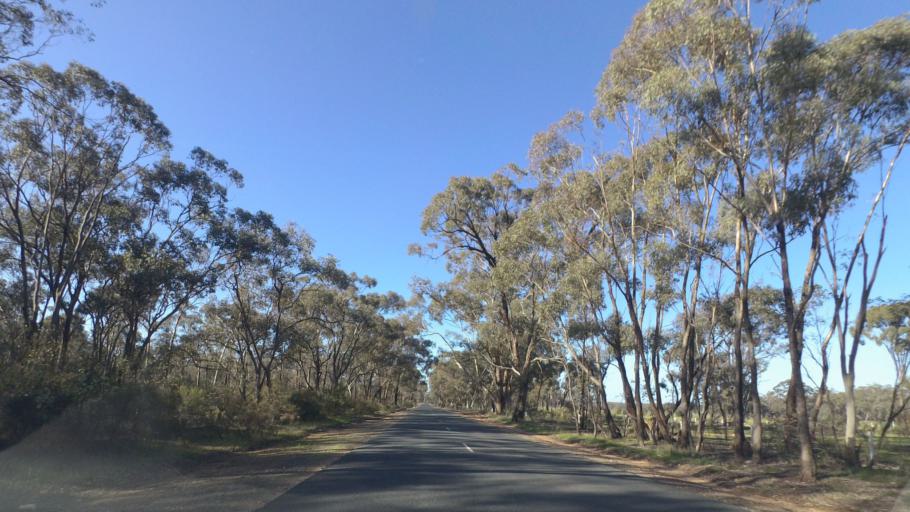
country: AU
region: Victoria
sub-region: Greater Bendigo
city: Epsom
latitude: -36.6634
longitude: 144.4489
